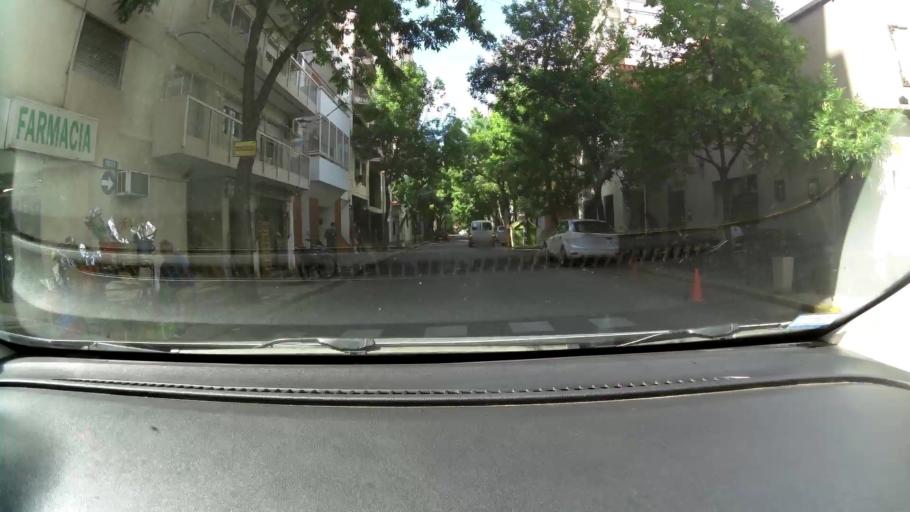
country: AR
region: Santa Fe
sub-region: Departamento de Rosario
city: Rosario
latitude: -32.9550
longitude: -60.6273
